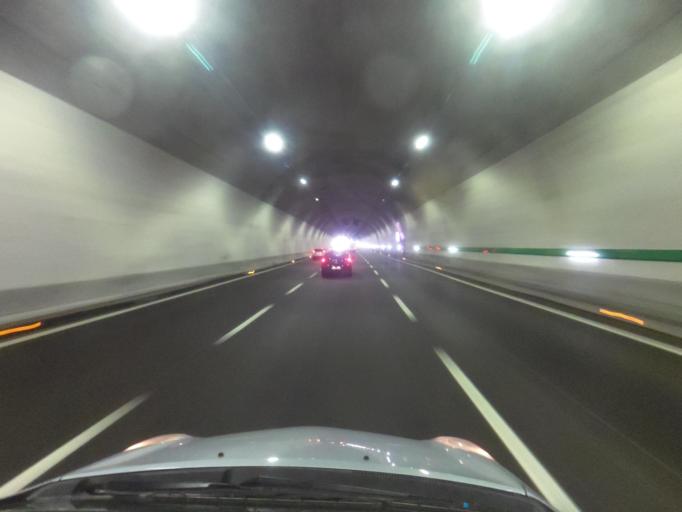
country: IT
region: Tuscany
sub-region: Province of Florence
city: Barberino di Mugello
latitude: 44.0013
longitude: 11.2126
